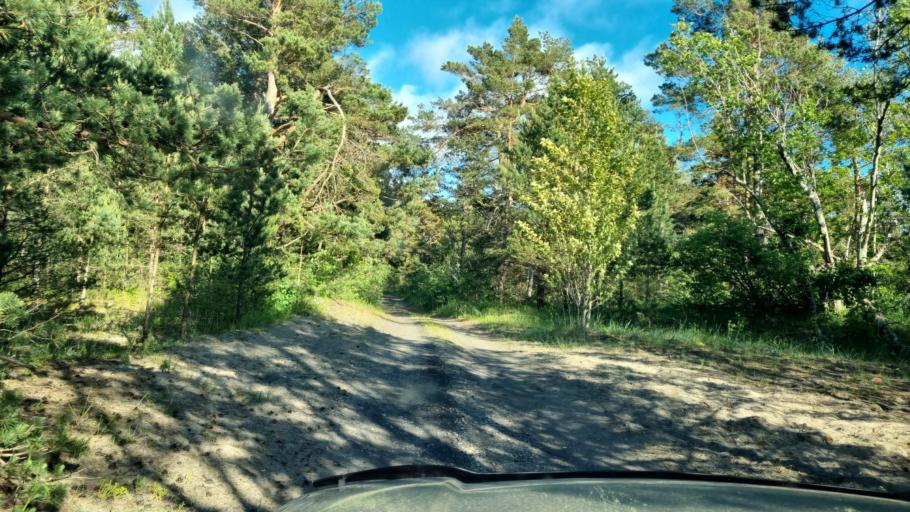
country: LV
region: Ventspils
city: Ventspils
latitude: 57.3640
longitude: 21.5097
